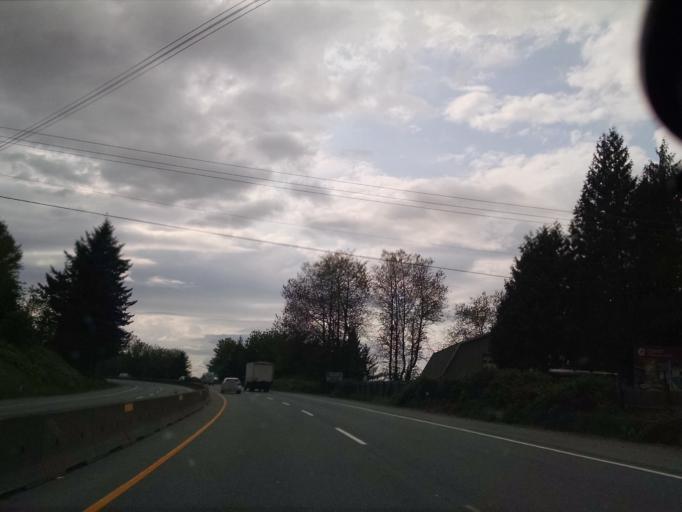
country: CA
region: British Columbia
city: Agassiz
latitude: 49.1607
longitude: -121.8073
